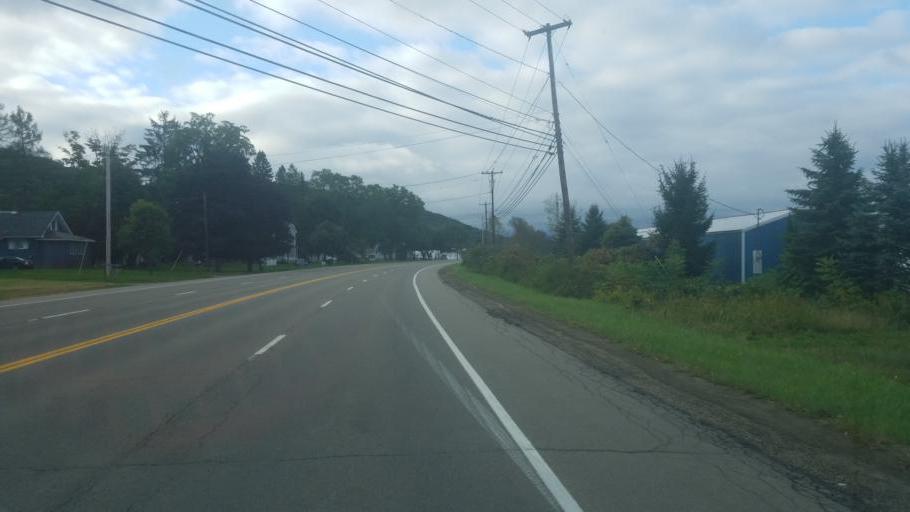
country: US
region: New York
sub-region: Cattaraugus County
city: Olean
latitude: 42.1163
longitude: -78.4151
